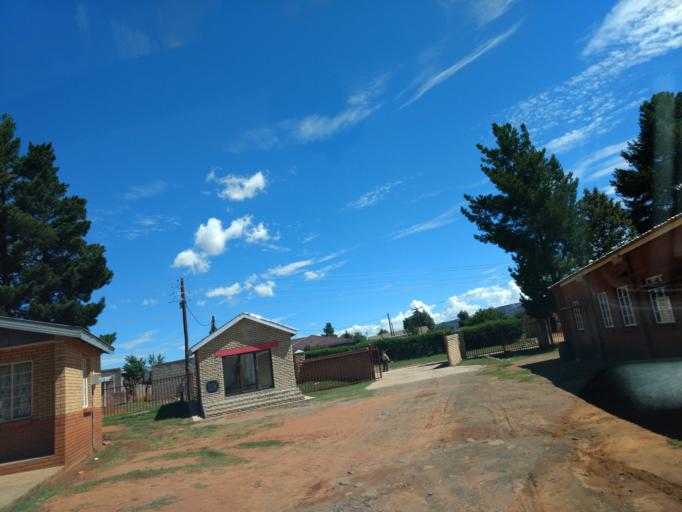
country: LS
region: Maseru
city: Maseru
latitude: -29.3719
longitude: 27.5065
